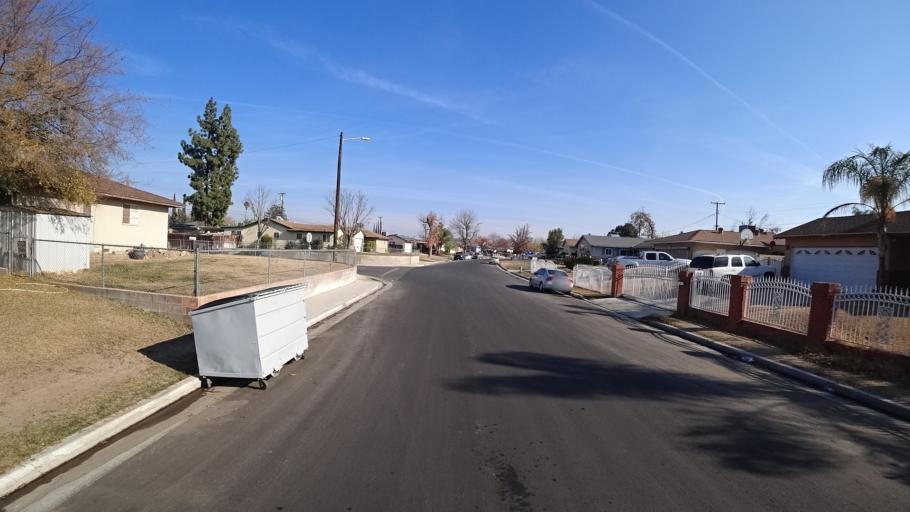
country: US
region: California
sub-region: Kern County
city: Bakersfield
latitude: 35.3282
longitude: -119.0178
